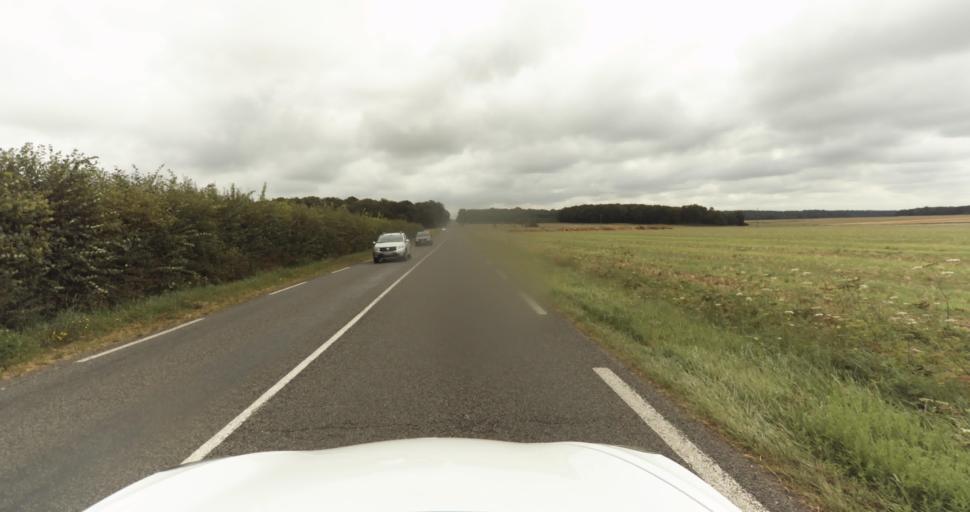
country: FR
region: Haute-Normandie
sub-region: Departement de l'Eure
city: Claville
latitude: 49.0357
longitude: 1.0506
